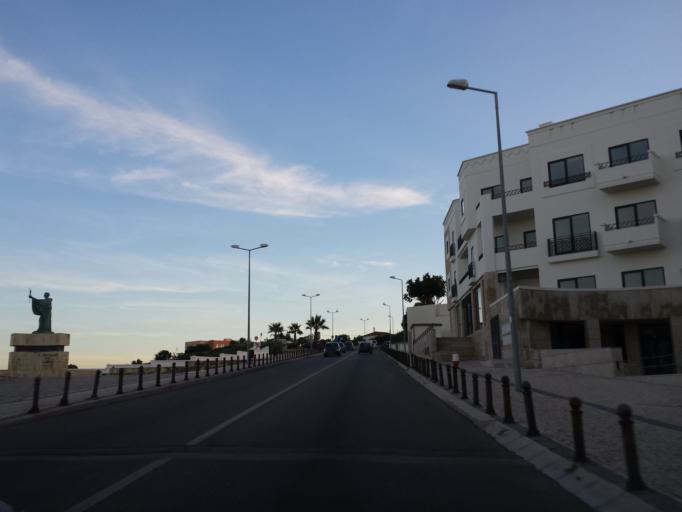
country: PT
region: Faro
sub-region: Lagos
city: Lagos
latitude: 37.0984
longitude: -8.6687
